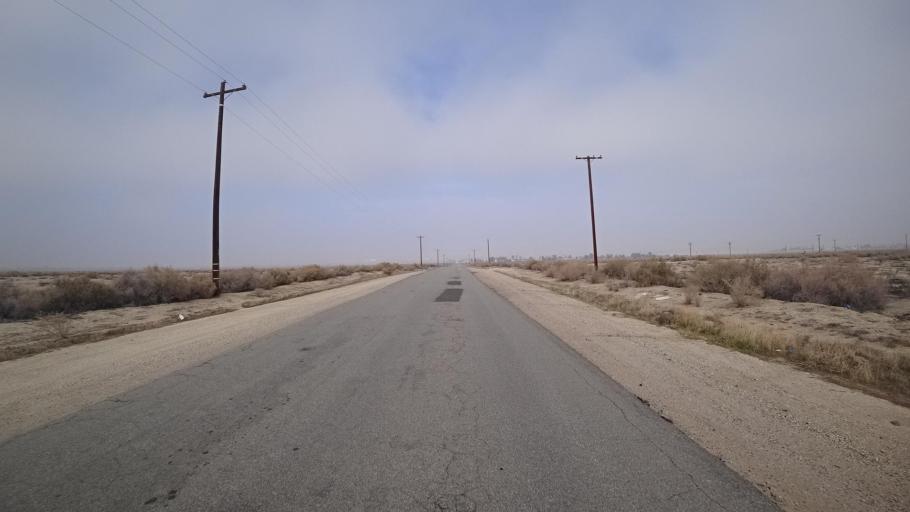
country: US
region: California
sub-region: Kern County
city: Ford City
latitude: 35.1995
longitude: -119.4290
